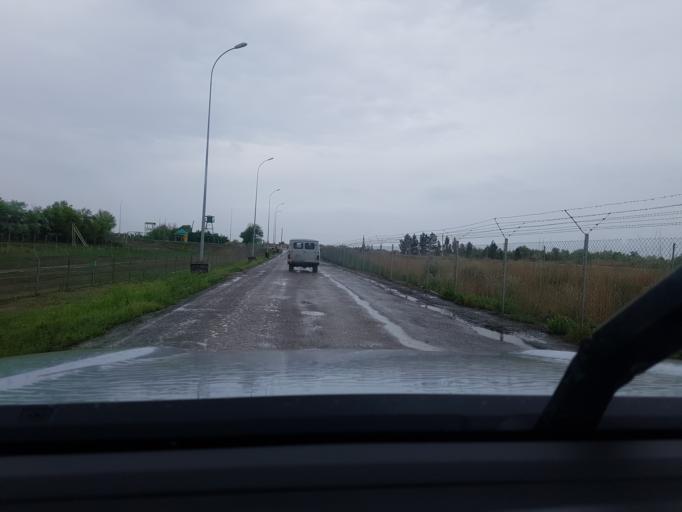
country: TM
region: Lebap
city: Farap
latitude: 39.2168
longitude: 63.7155
